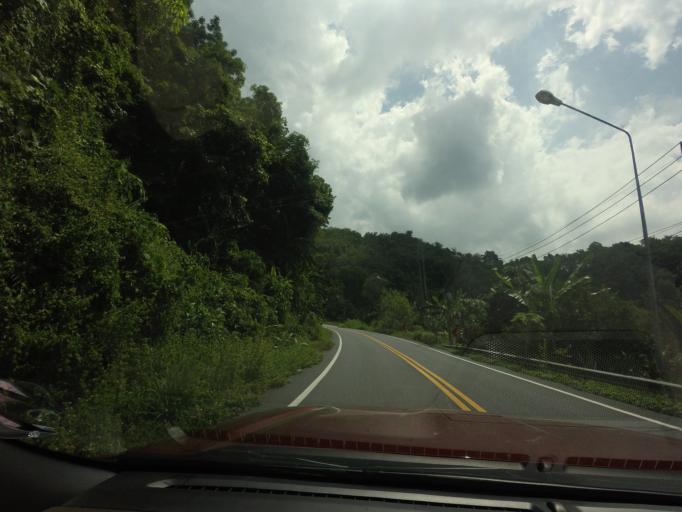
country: TH
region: Yala
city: Than To
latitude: 6.0340
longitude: 101.2079
